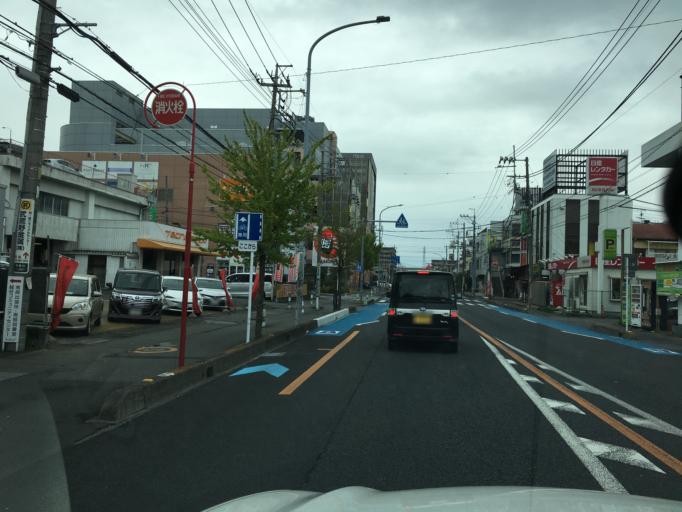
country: JP
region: Saitama
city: Koshigaya
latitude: 35.8739
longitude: 139.7937
